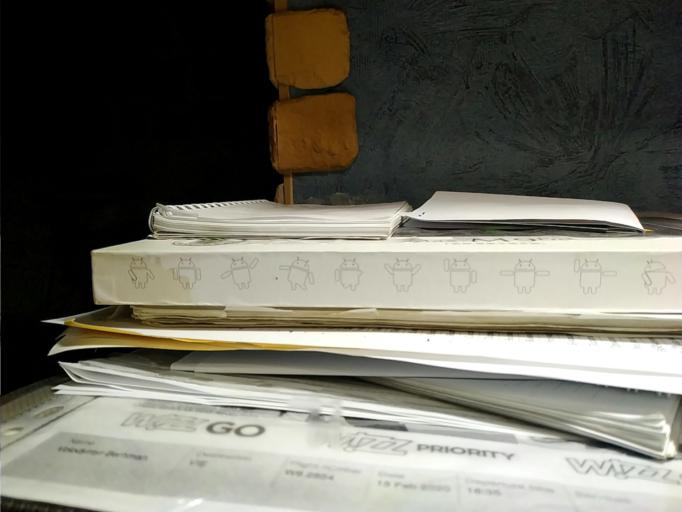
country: RU
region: Arkhangelskaya
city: Konevo
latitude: 62.8180
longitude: 38.5472
